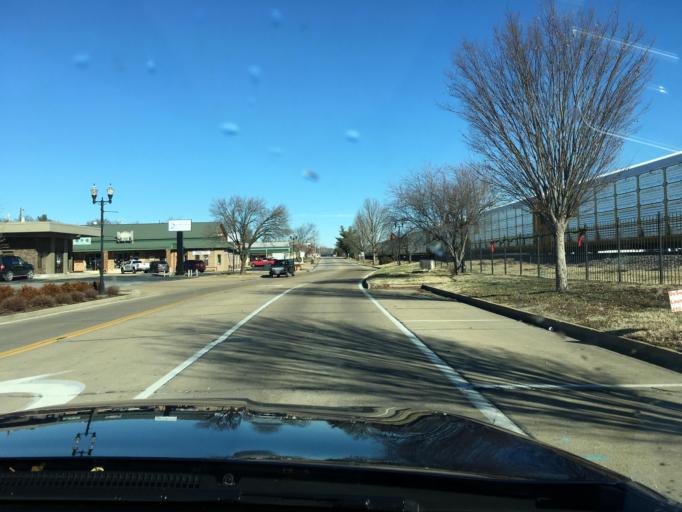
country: US
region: Missouri
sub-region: Jefferson County
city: De Soto
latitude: 38.1421
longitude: -90.5526
